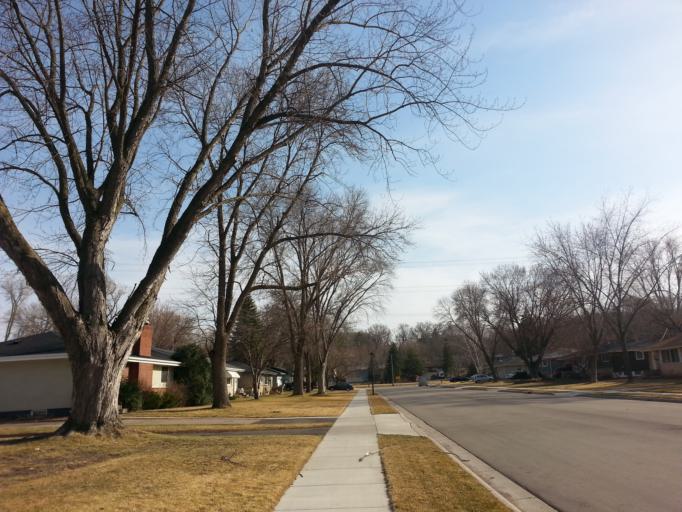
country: US
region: Minnesota
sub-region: Scott County
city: Savage
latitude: 44.7729
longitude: -93.3369
